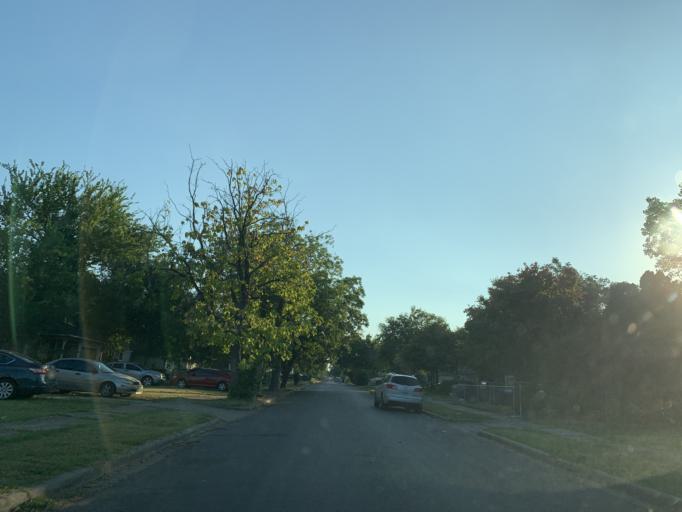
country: US
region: Texas
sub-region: Dallas County
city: Dallas
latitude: 32.7088
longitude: -96.7878
